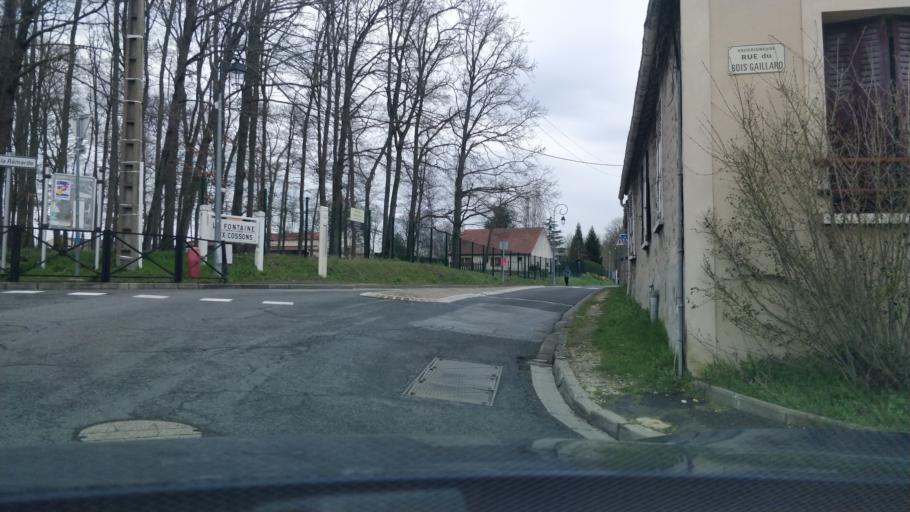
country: FR
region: Ile-de-France
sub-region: Departement de l'Essonne
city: Vaugrigneuse
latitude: 48.5915
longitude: 2.1106
